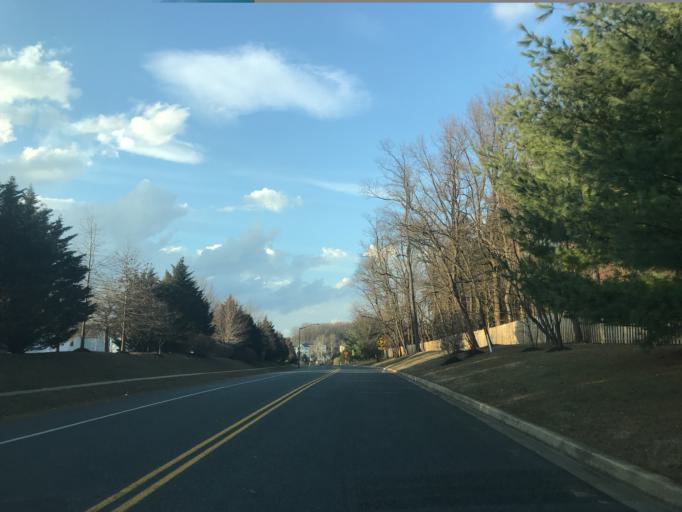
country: US
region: Maryland
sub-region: Harford County
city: Bel Air South
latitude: 39.4795
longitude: -76.3274
